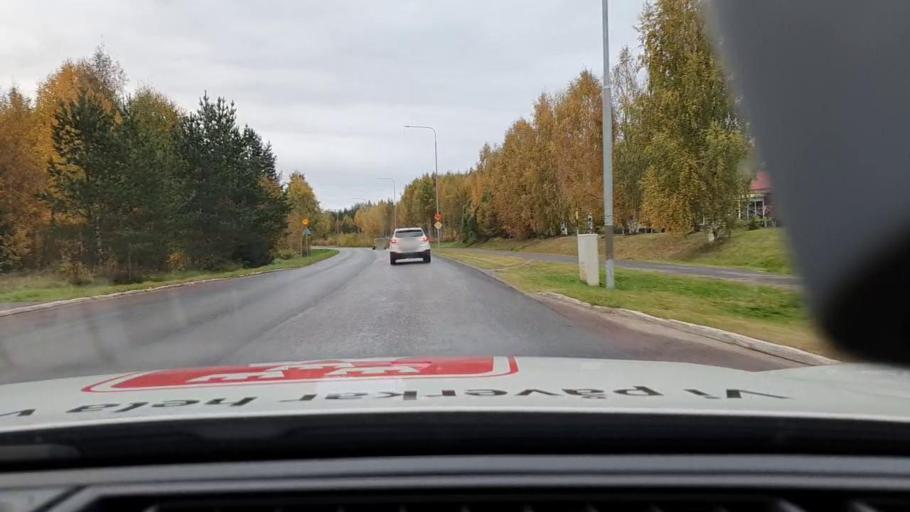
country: SE
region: Norrbotten
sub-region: Bodens Kommun
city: Saevast
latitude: 65.7617
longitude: 21.7388
